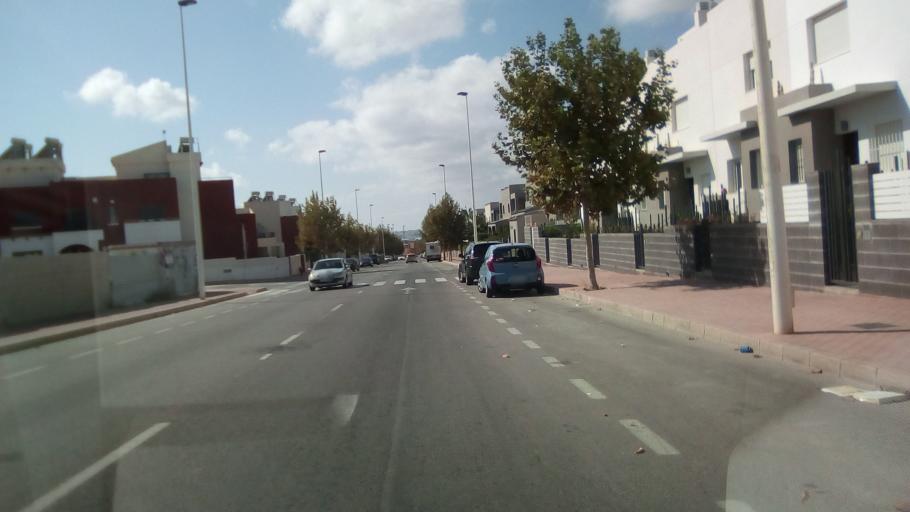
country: ES
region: Valencia
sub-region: Provincia de Alicante
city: Torrevieja
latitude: 38.0021
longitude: -0.6745
